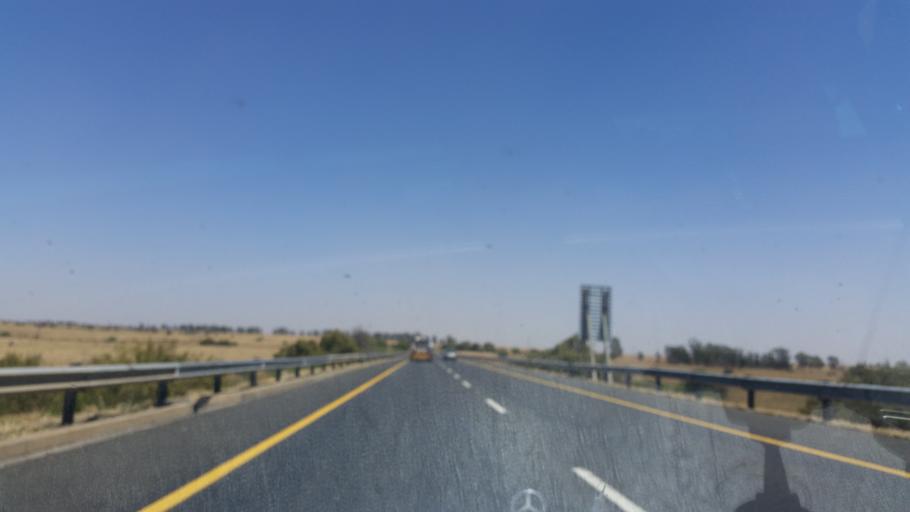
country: ZA
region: Orange Free State
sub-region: Lejweleputswa District Municipality
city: Winburg
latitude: -28.6327
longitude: 26.9021
